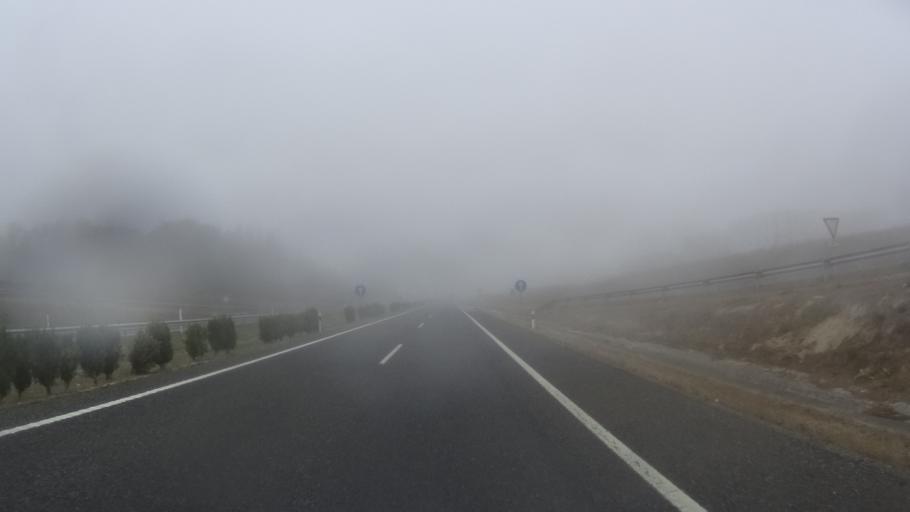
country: ES
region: Galicia
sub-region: Provincia de Lugo
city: Corgo
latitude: 42.9401
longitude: -7.3976
